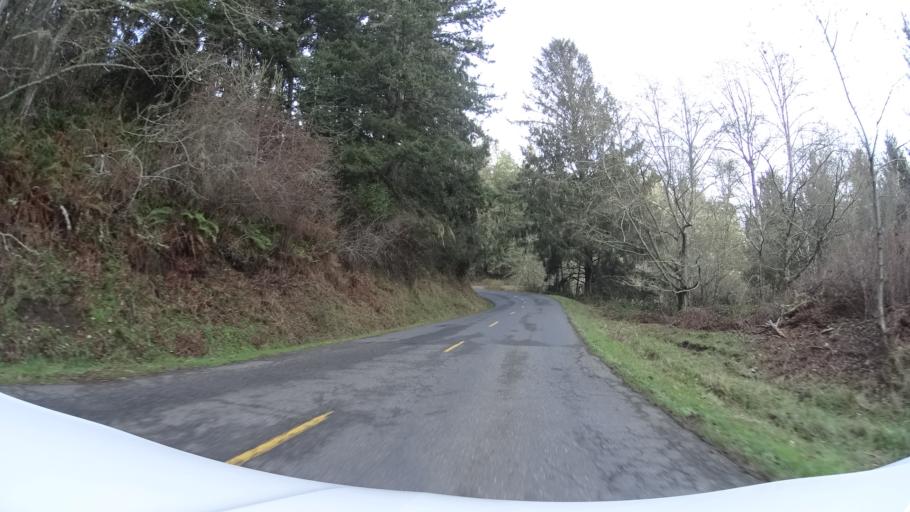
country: US
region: California
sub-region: Humboldt County
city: Ferndale
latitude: 40.5717
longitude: -124.2699
